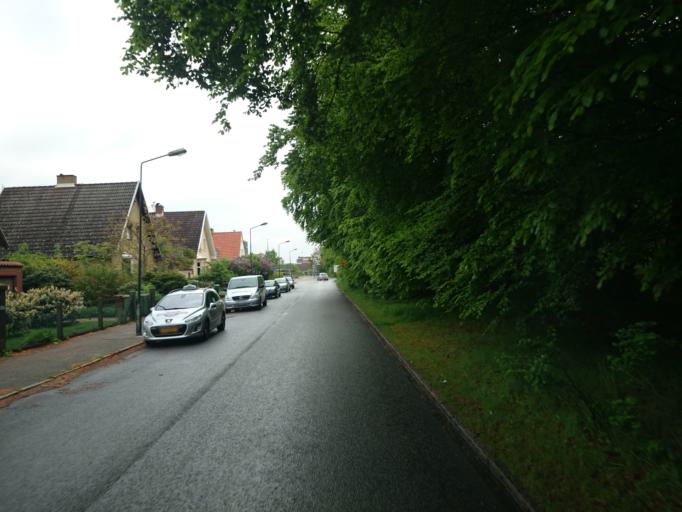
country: SE
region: Skane
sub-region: Burlovs Kommun
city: Arloev
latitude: 55.6117
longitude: 13.0495
